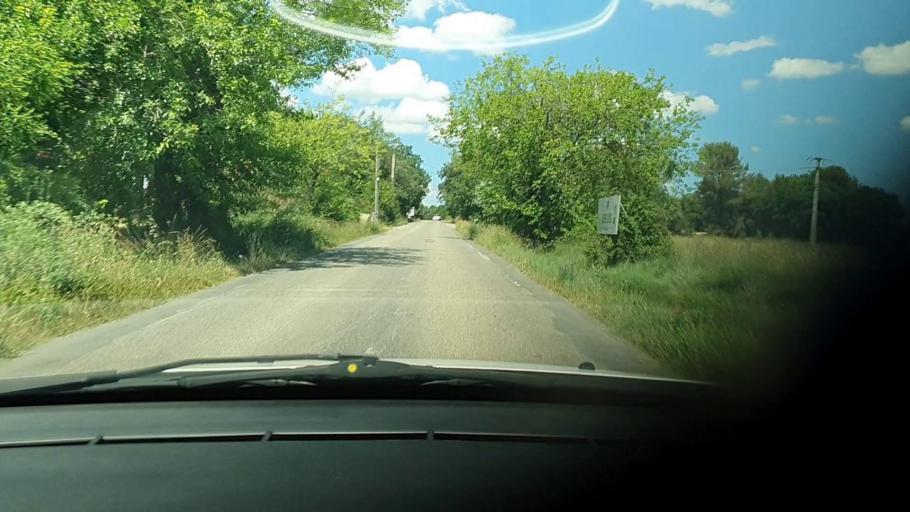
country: FR
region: Languedoc-Roussillon
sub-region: Departement du Gard
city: Blauzac
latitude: 43.9771
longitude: 4.3708
